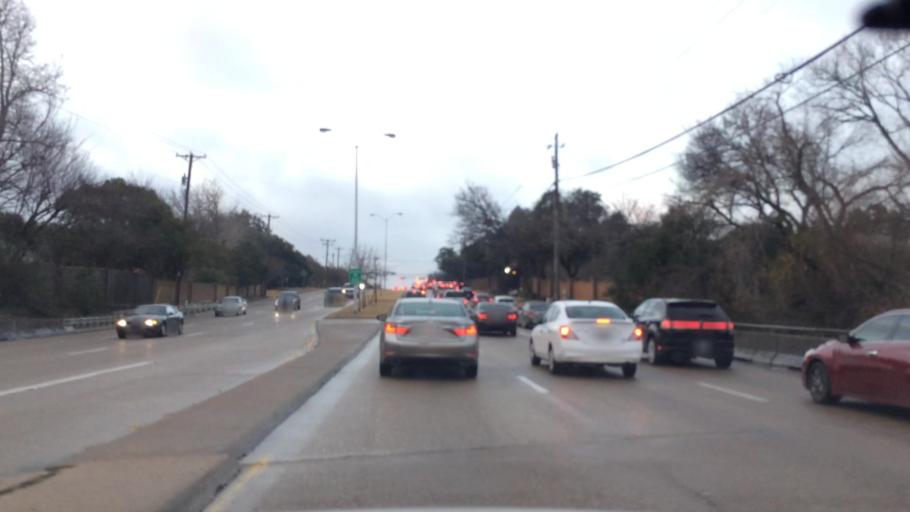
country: US
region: Texas
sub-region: Dallas County
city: Addison
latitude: 32.9648
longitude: -96.8045
